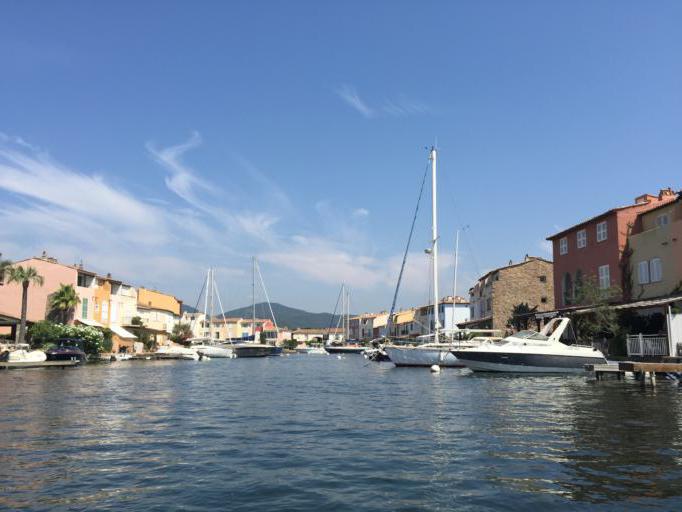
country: FR
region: Provence-Alpes-Cote d'Azur
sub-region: Departement du Var
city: Gassin
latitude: 43.2739
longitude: 6.5832
